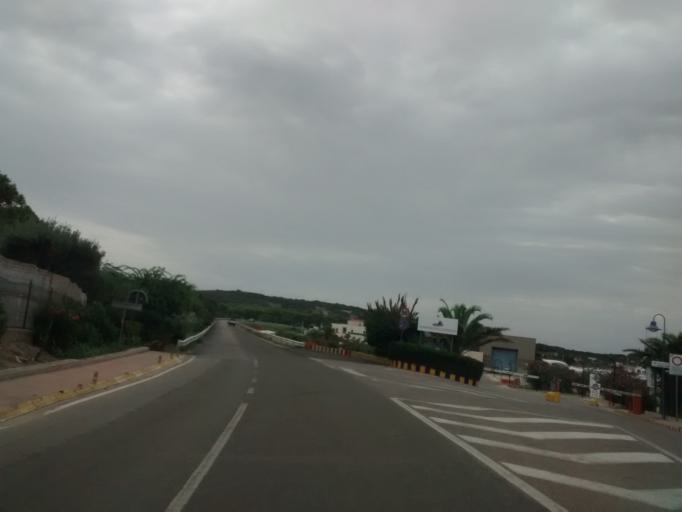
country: IT
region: Sardinia
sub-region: Provincia di Cagliari
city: Villasimius
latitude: 39.1201
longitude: 9.5105
